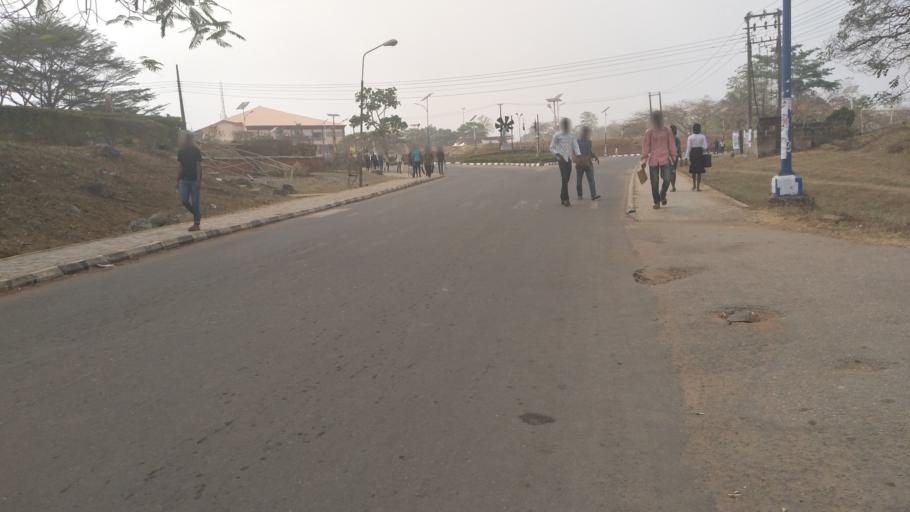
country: NG
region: Ondo
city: Ilare
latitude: 7.3031
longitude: 5.1393
